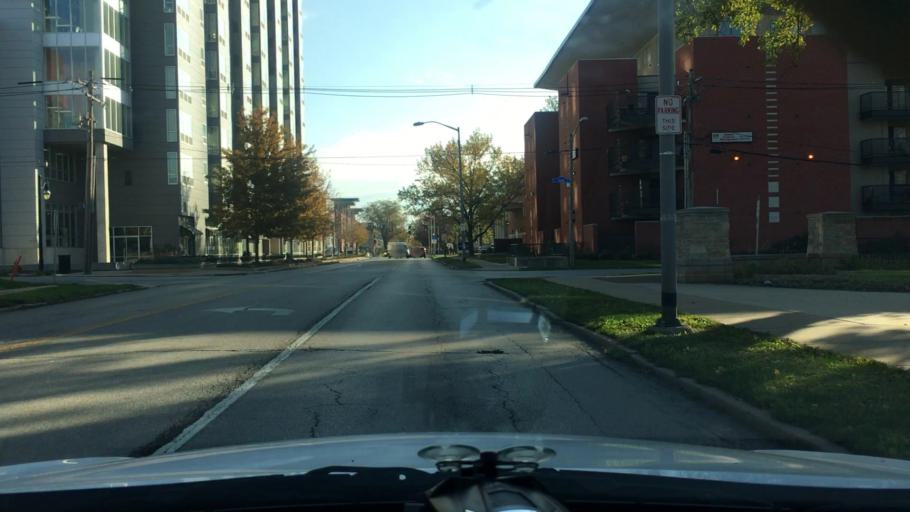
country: US
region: Illinois
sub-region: Champaign County
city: Champaign
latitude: 40.1126
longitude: -88.2358
